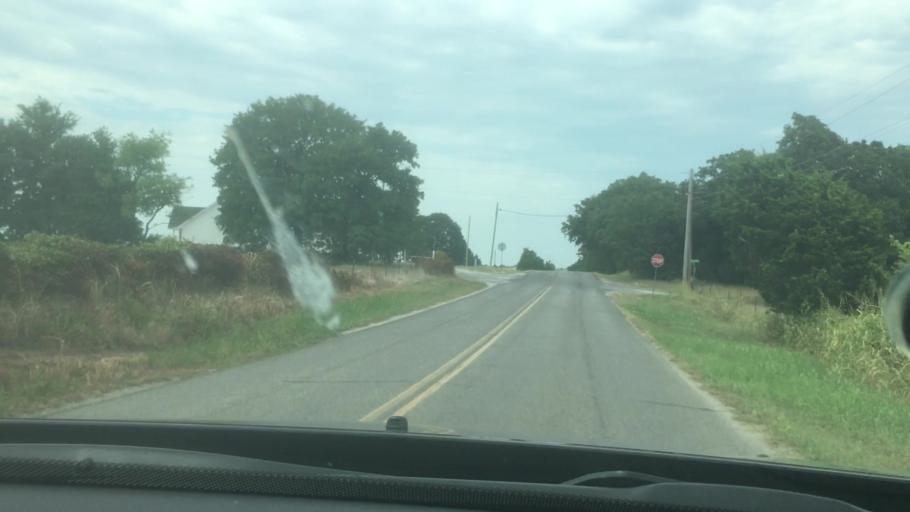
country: US
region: Oklahoma
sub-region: Murray County
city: Davis
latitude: 34.4910
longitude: -97.0555
